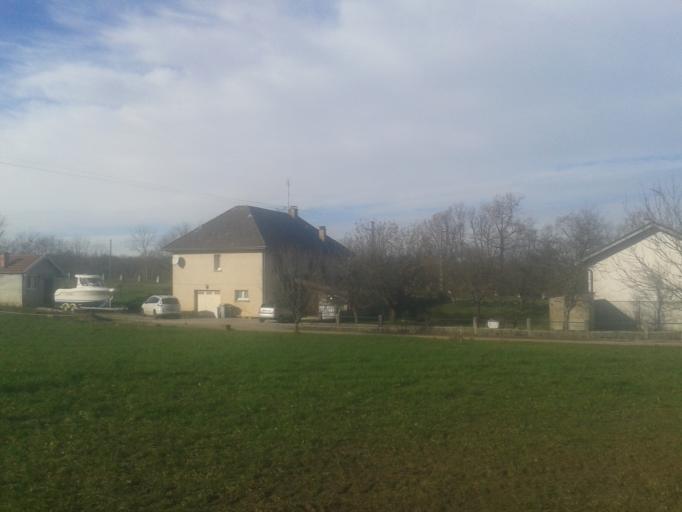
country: FR
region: Franche-Comte
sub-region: Departement du Doubs
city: Levier
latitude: 47.0047
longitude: 6.0282
